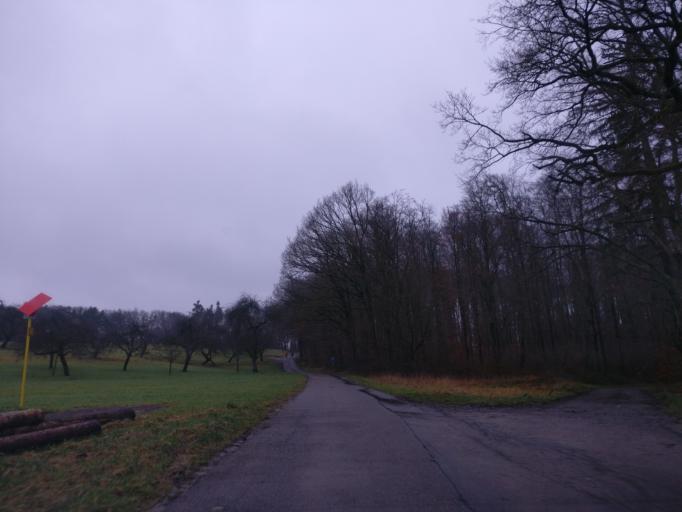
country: DE
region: Baden-Wuerttemberg
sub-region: Regierungsbezirk Stuttgart
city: Rudersberg
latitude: 48.8752
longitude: 9.4943
